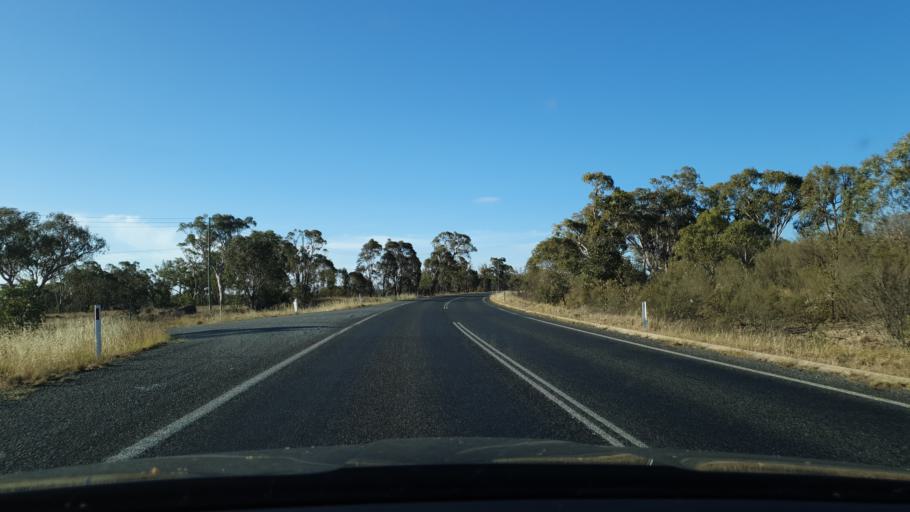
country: AU
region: Queensland
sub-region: Southern Downs
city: Stanthorpe
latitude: -28.6687
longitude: 151.9160
